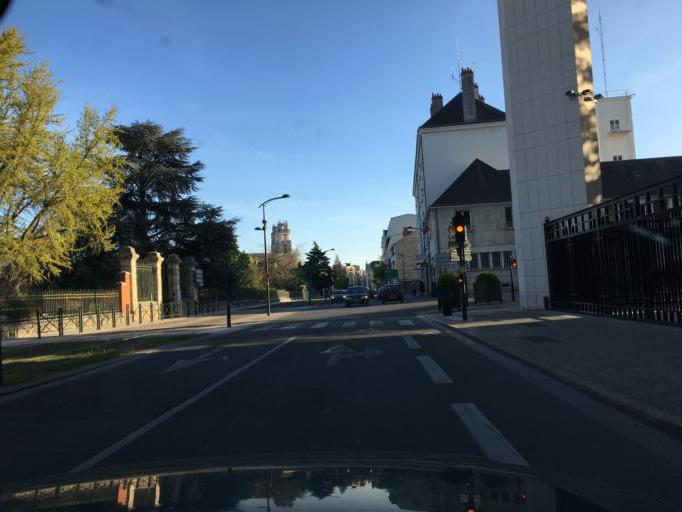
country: FR
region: Centre
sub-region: Departement du Loiret
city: Orleans
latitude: 47.9079
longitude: 1.9105
